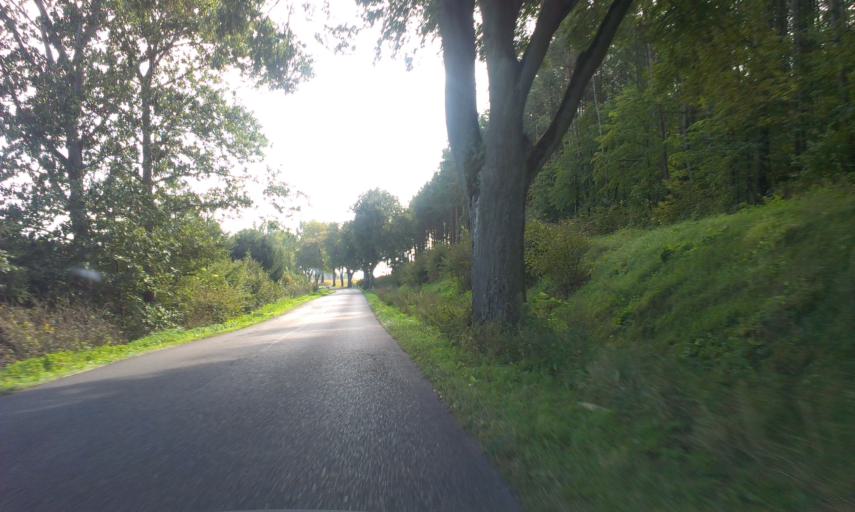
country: PL
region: Greater Poland Voivodeship
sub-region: Powiat zlotowski
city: Zlotow
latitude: 53.3931
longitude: 17.0020
